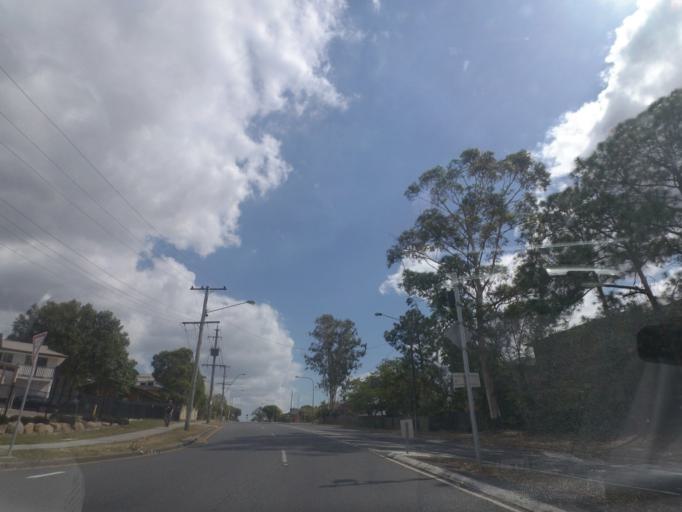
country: AU
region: Queensland
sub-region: Brisbane
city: Upper Mount Gravatt
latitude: -27.5662
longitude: 153.0880
